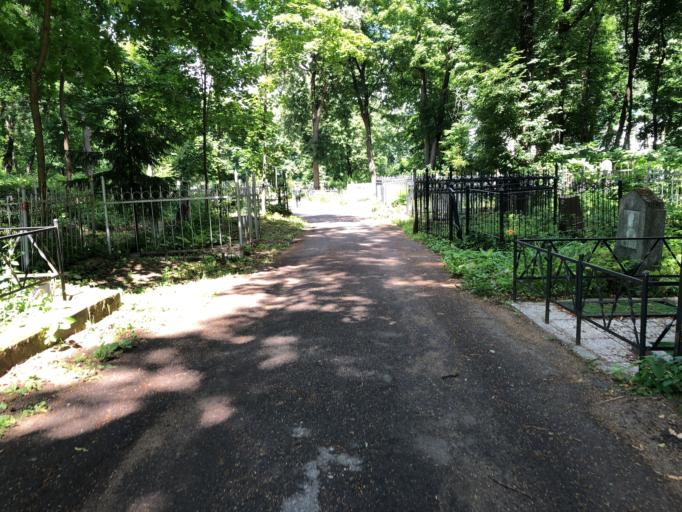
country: RU
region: Tula
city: Tula
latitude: 54.1797
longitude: 37.6109
